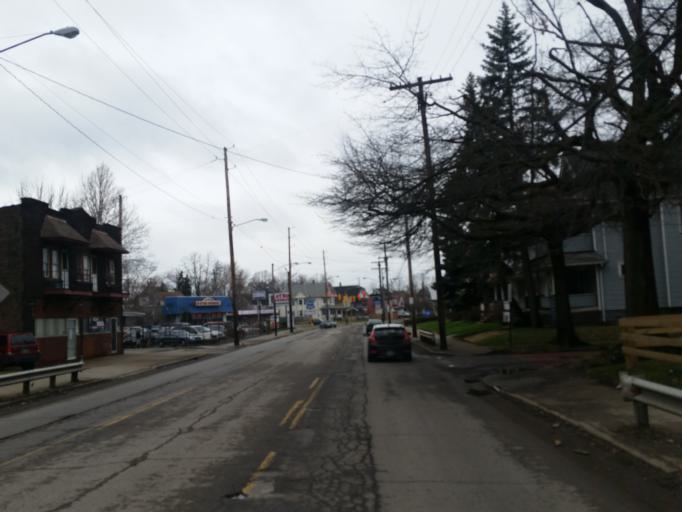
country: US
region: Ohio
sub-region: Cuyahoga County
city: Newburgh Heights
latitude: 41.4485
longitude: -81.6417
